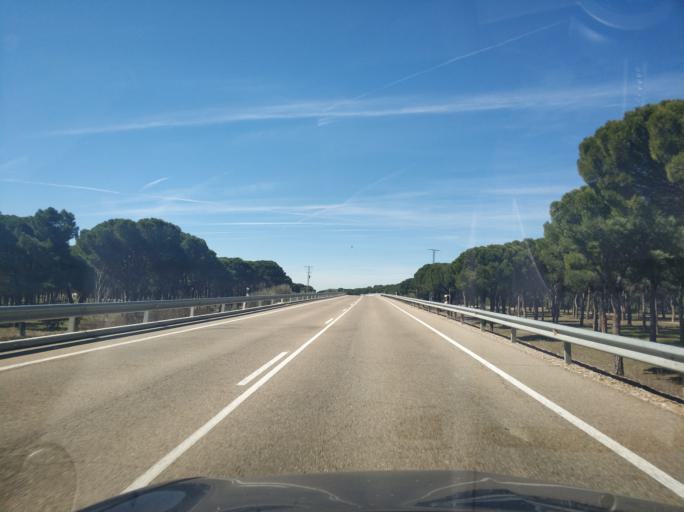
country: ES
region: Castille and Leon
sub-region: Provincia de Valladolid
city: Viana de Cega
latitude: 41.5330
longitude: -4.7335
